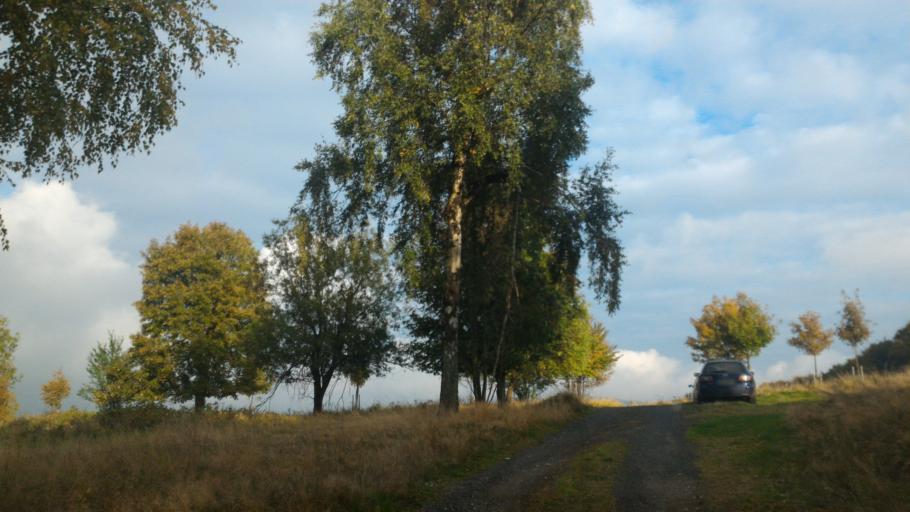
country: CZ
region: Ustecky
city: Dolni Podluzi
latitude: 50.8649
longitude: 14.5650
